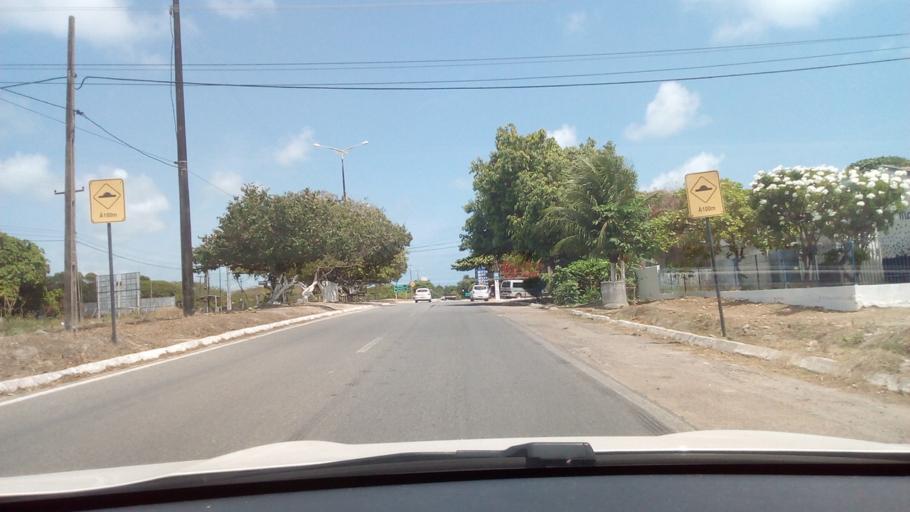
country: BR
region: Paraiba
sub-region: Joao Pessoa
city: Joao Pessoa
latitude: -7.1633
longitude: -34.8006
